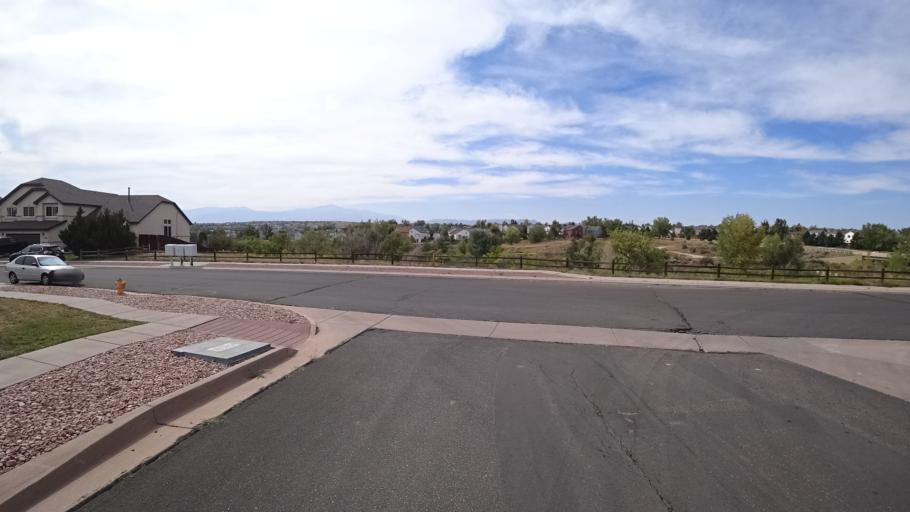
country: US
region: Colorado
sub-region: El Paso County
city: Cimarron Hills
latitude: 38.9103
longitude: -104.7011
